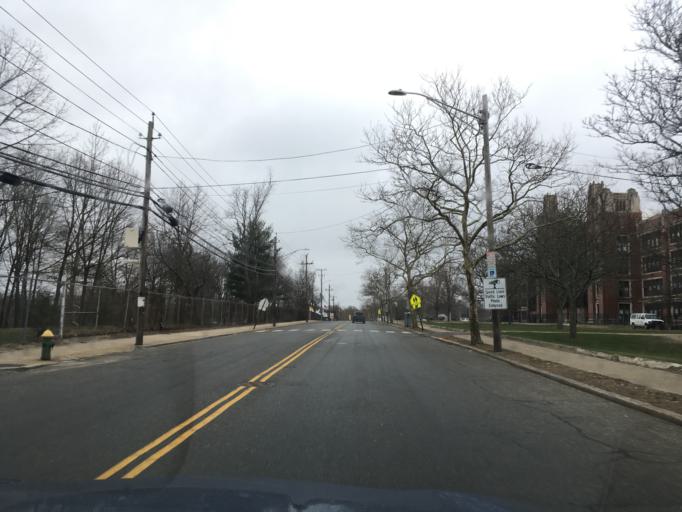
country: US
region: Rhode Island
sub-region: Providence County
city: North Providence
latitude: 41.8409
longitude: -71.4525
